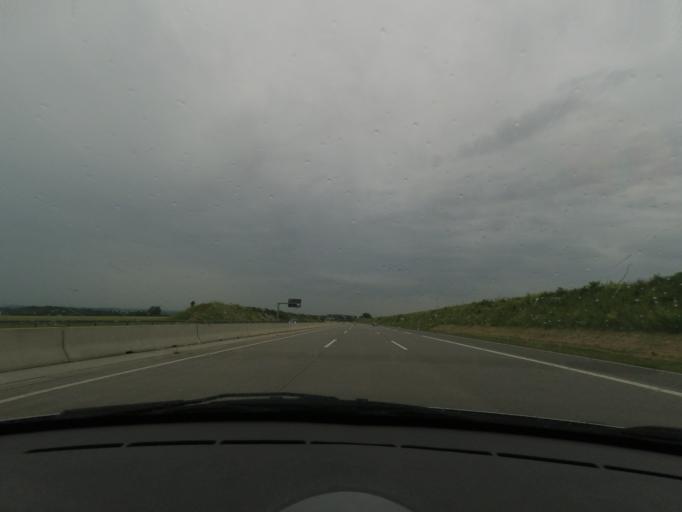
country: DE
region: Thuringia
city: Heyersdorf
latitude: 50.8482
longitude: 12.3388
